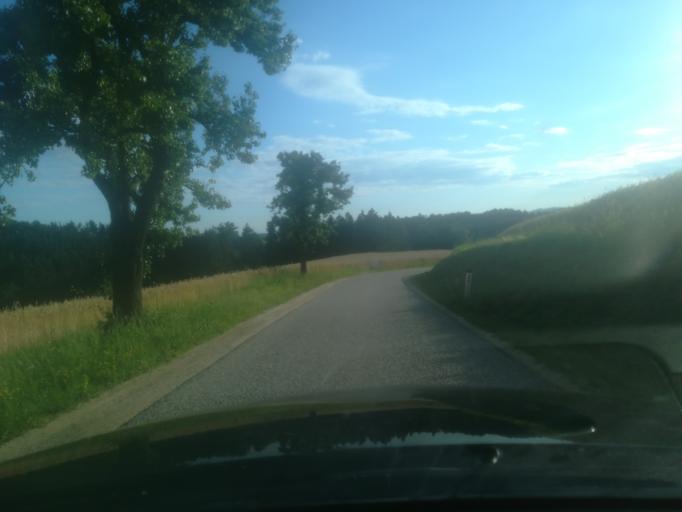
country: AT
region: Upper Austria
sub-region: Politischer Bezirk Perg
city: Perg
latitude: 48.3494
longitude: 14.5660
